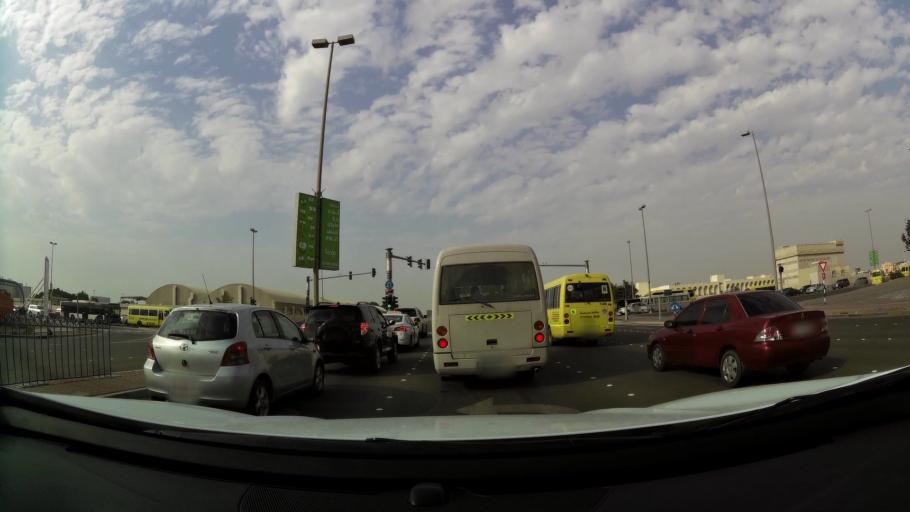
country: AE
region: Abu Dhabi
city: Abu Dhabi
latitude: 24.3738
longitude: 54.5364
